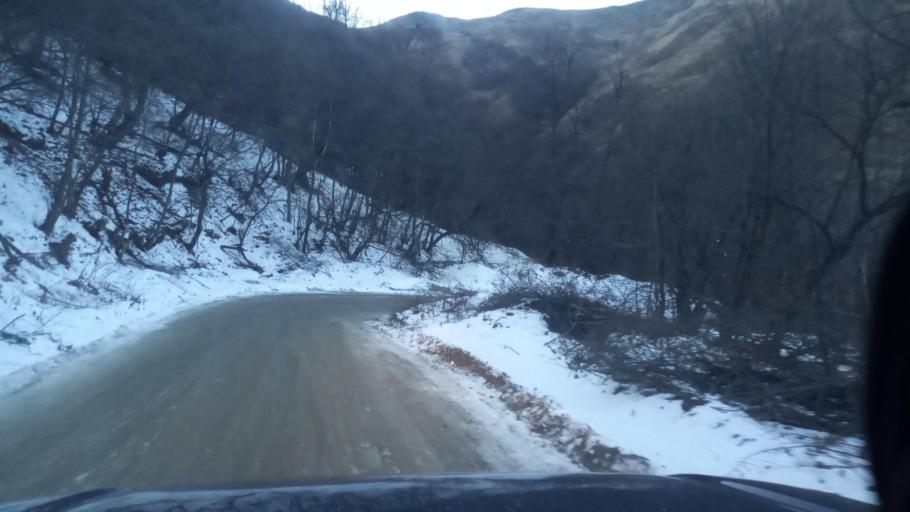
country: RU
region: Ingushetiya
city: Dzhayrakh
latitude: 42.8300
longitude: 44.5823
